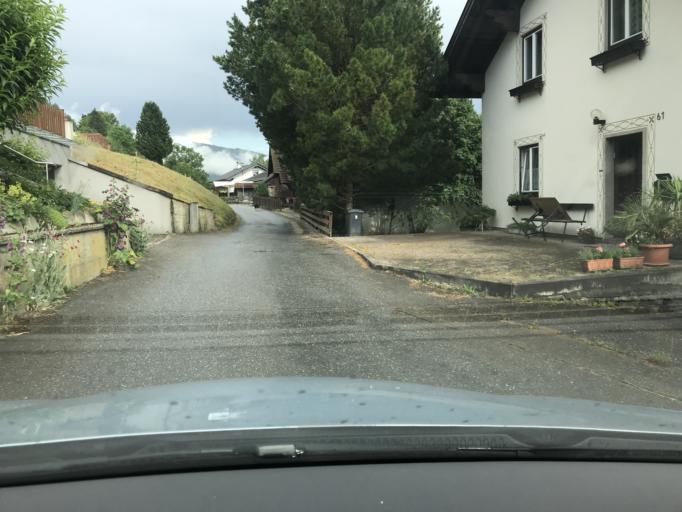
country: AT
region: Styria
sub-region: Politischer Bezirk Murau
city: Sankt Peter am Kammersberg
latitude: 47.1874
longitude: 14.1908
